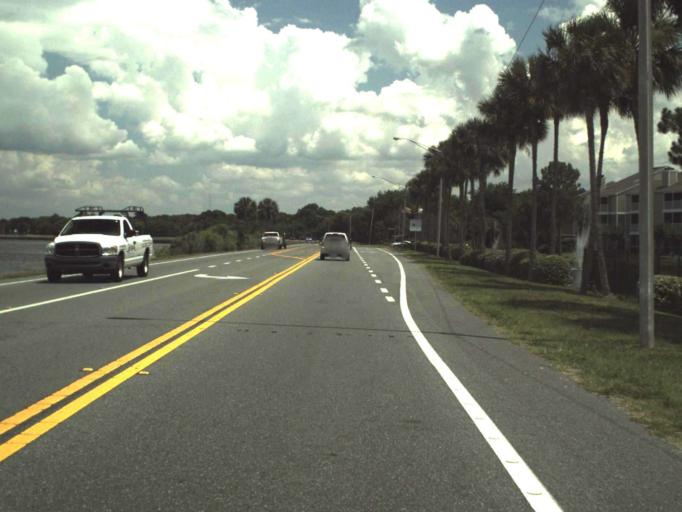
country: US
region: Florida
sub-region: Seminole County
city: Sanford
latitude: 28.8201
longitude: -81.2911
